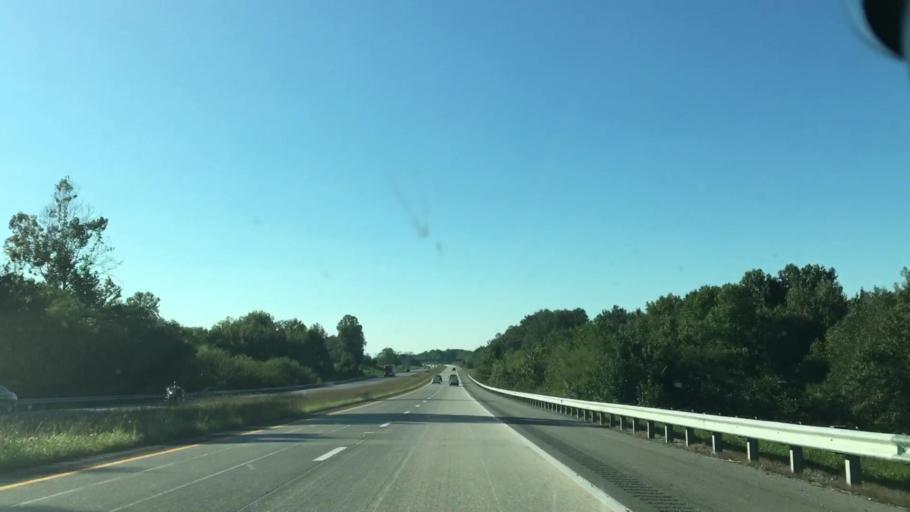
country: US
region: Indiana
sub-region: Warrick County
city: Newburgh
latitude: 37.7641
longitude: -87.4210
